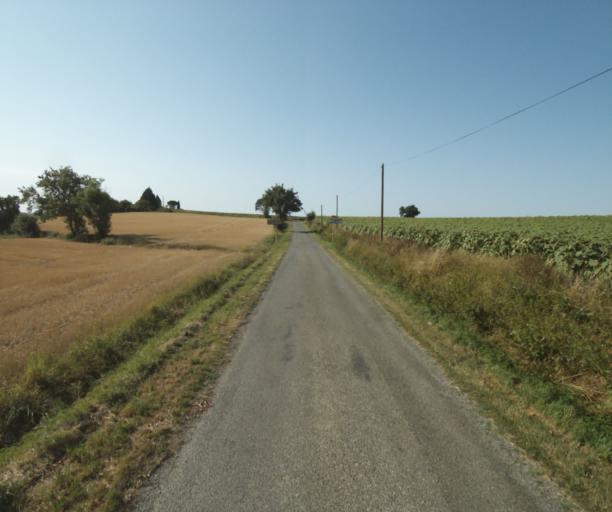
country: FR
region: Midi-Pyrenees
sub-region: Departement de la Haute-Garonne
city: Avignonet-Lauragais
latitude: 43.4276
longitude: 1.8169
